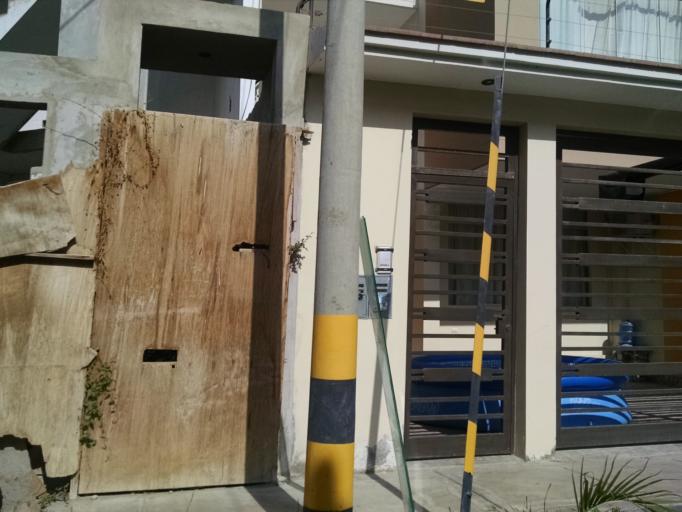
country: PE
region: Piura
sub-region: Provincia de Piura
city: Piura
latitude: -5.1704
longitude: -80.6310
